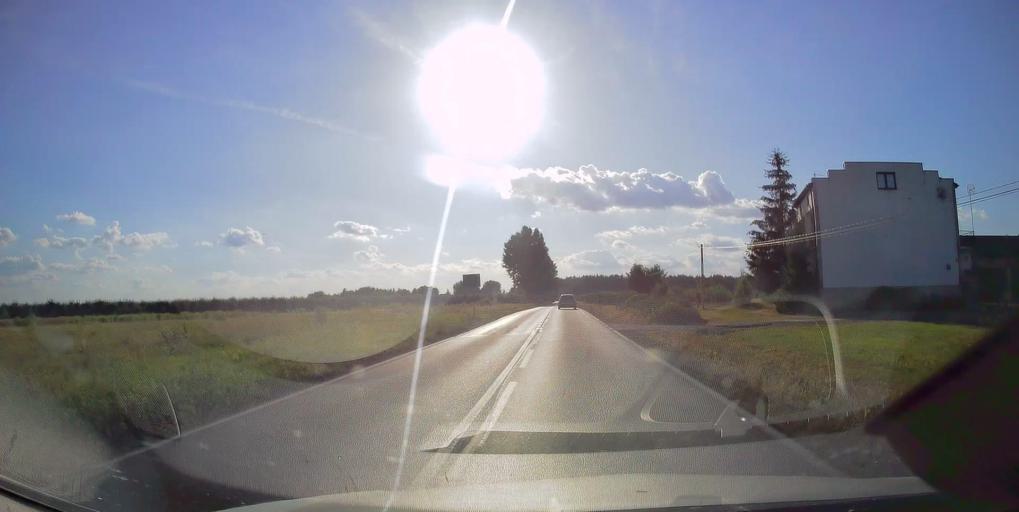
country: PL
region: Masovian Voivodeship
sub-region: Powiat grojecki
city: Bledow
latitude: 51.8106
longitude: 20.7215
